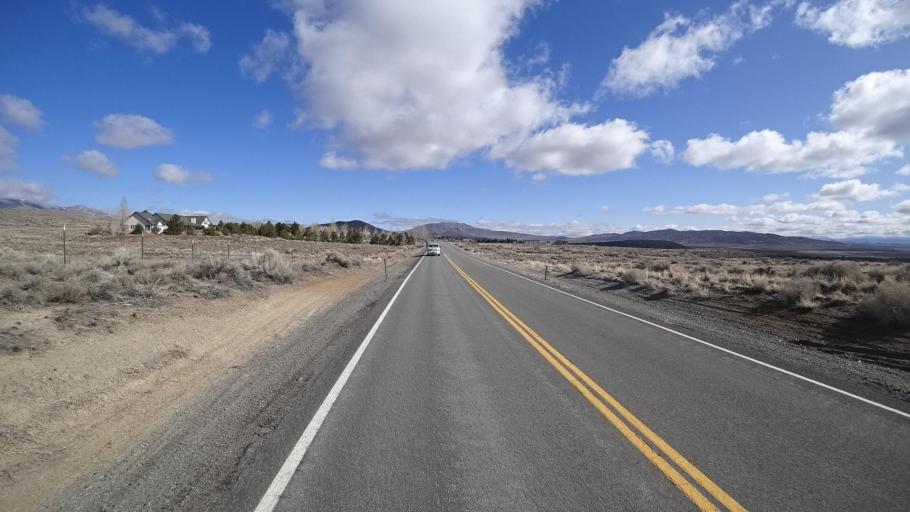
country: US
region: Nevada
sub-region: Washoe County
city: Cold Springs
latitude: 39.6822
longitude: -119.9217
